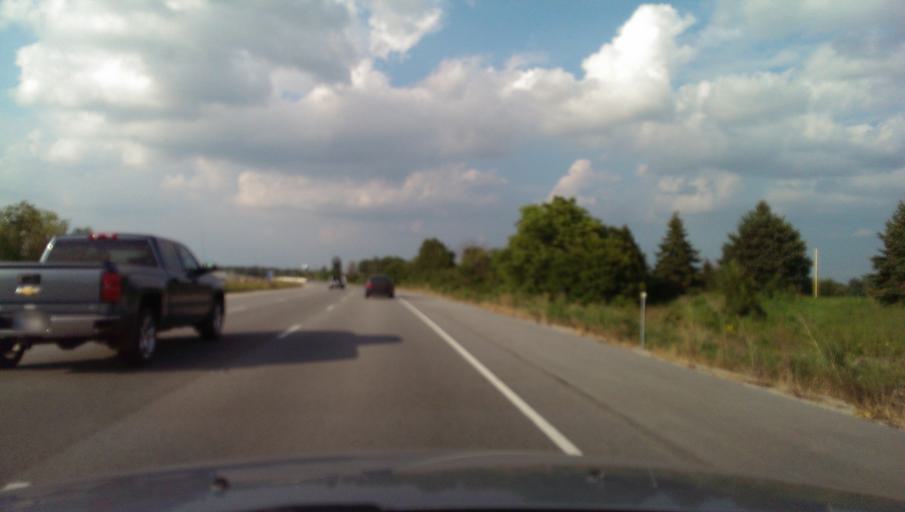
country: US
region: Indiana
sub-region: Hamilton County
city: Westfield
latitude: 40.0572
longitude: -86.1297
